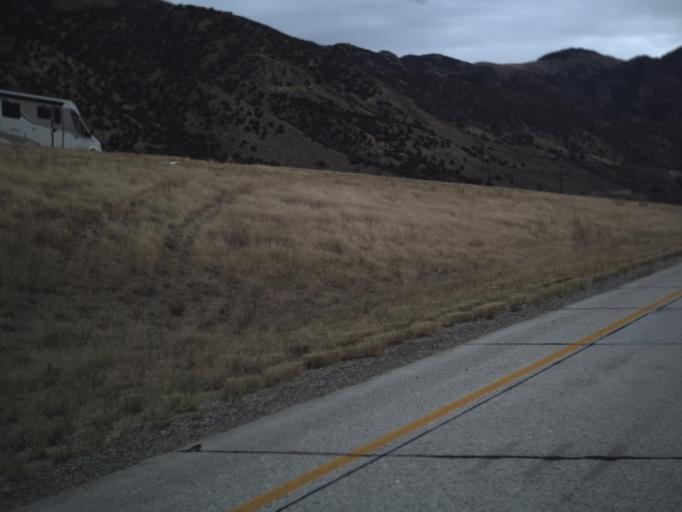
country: US
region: Idaho
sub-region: Oneida County
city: Malad City
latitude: 41.9760
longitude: -112.1900
